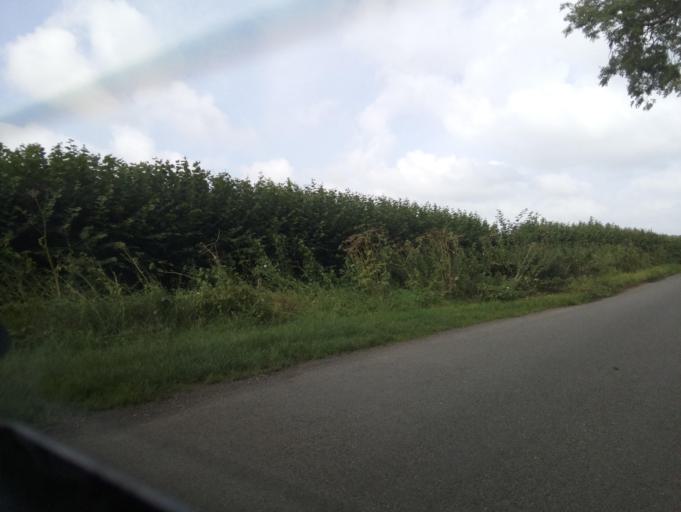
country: GB
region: England
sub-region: Bath and North East Somerset
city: Cameley
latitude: 51.2660
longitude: -2.5780
